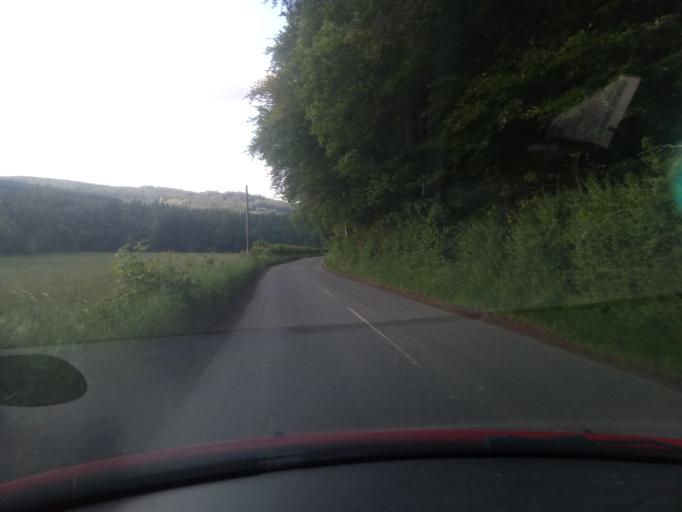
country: GB
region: Scotland
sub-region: The Scottish Borders
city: Selkirk
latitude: 55.5196
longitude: -2.9241
